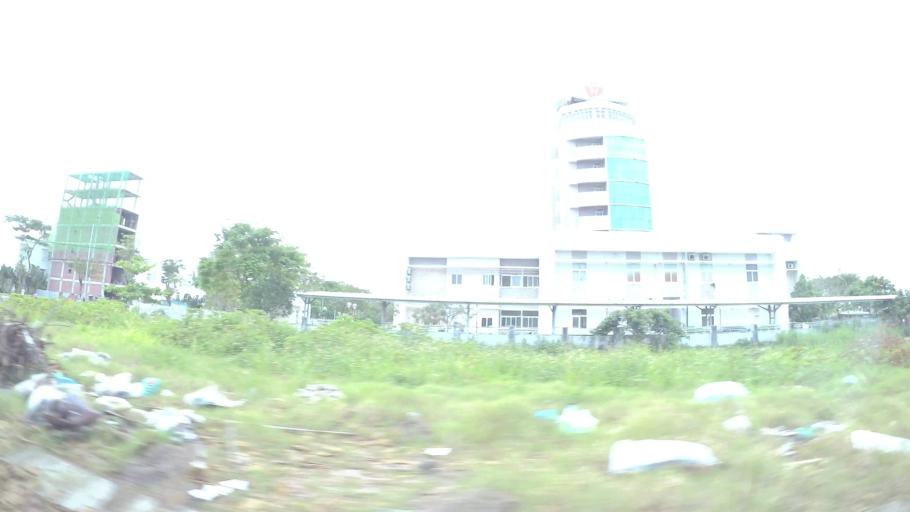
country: VN
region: Da Nang
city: Son Tra
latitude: 16.0572
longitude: 108.2324
